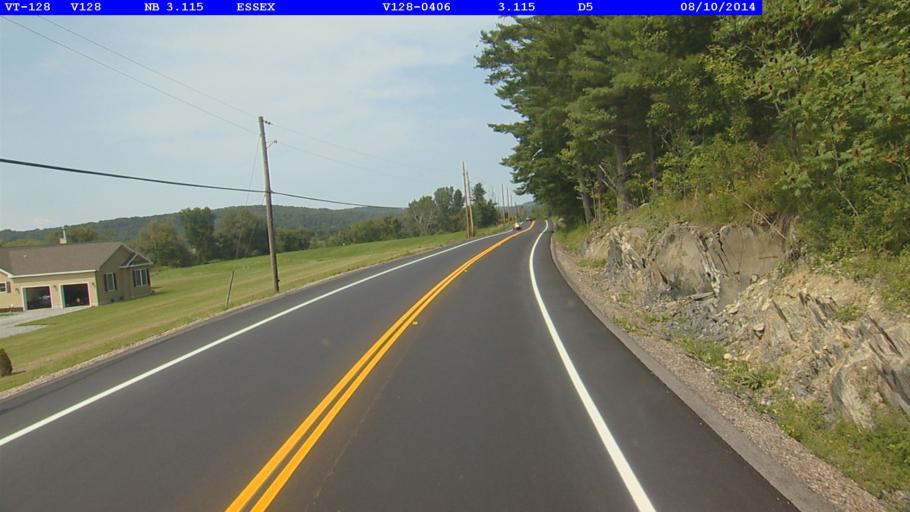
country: US
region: Vermont
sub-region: Chittenden County
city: Jericho
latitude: 44.5425
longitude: -73.0329
